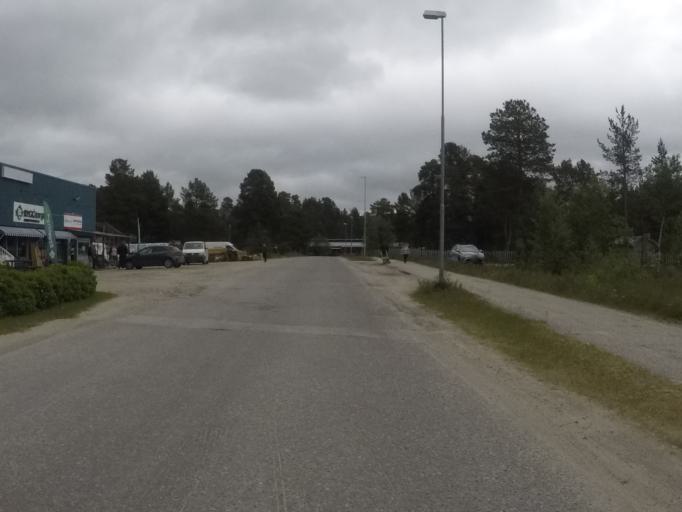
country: NO
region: Finnmark Fylke
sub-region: Karasjok
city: Karasjohka
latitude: 69.4722
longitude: 25.5228
